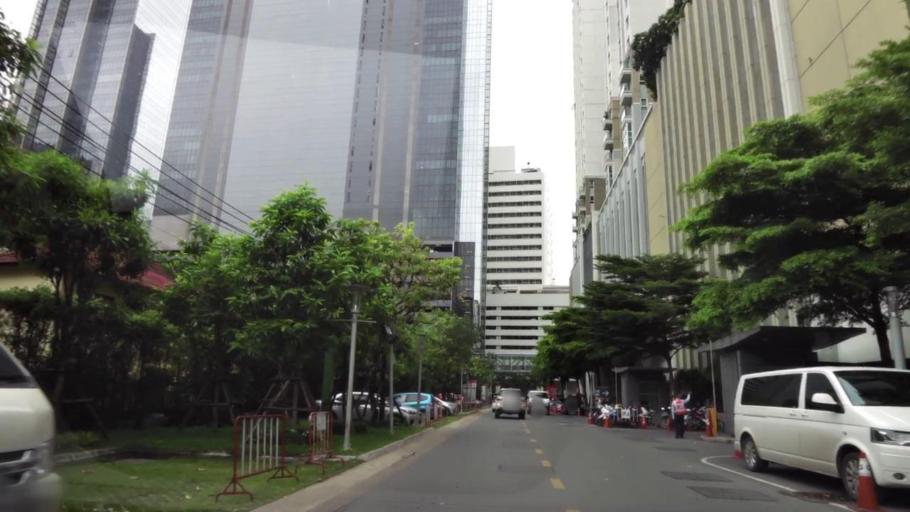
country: TH
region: Bangkok
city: Din Daeng
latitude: 13.7595
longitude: 100.5694
